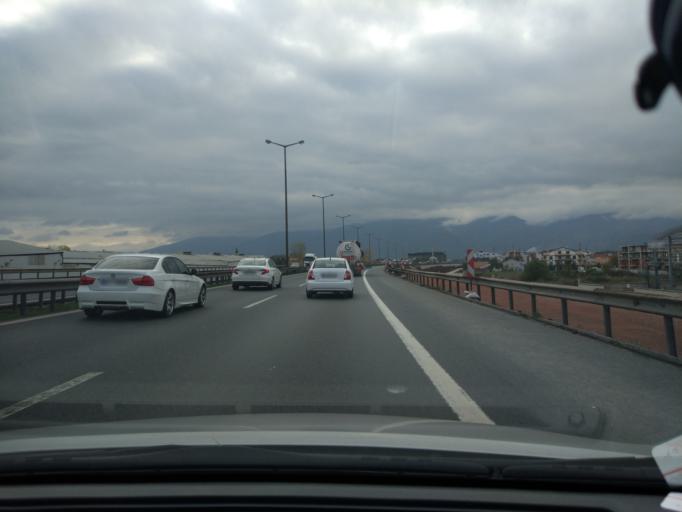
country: TR
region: Kocaeli
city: Kosekoy
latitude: 40.7597
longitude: 30.0352
